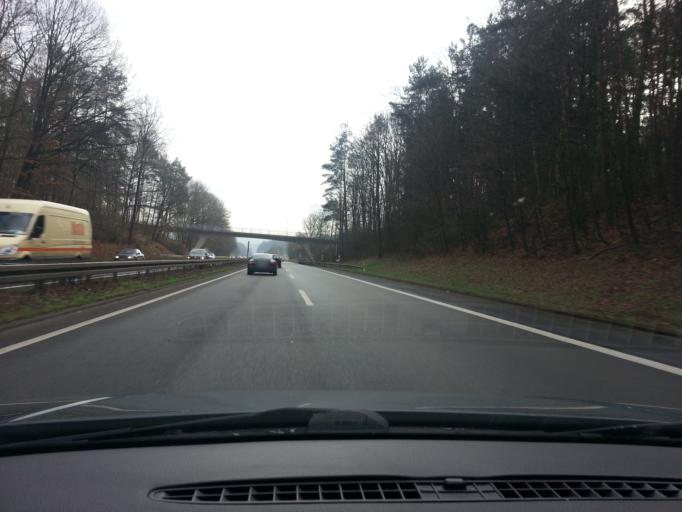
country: DE
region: Saarland
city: Kirkel
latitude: 49.3020
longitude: 7.2789
